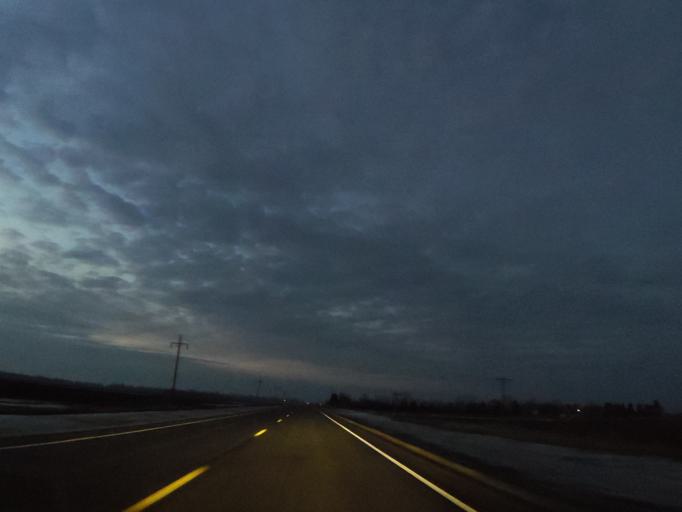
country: US
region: North Dakota
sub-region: Walsh County
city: Park River
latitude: 48.2783
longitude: -97.6225
